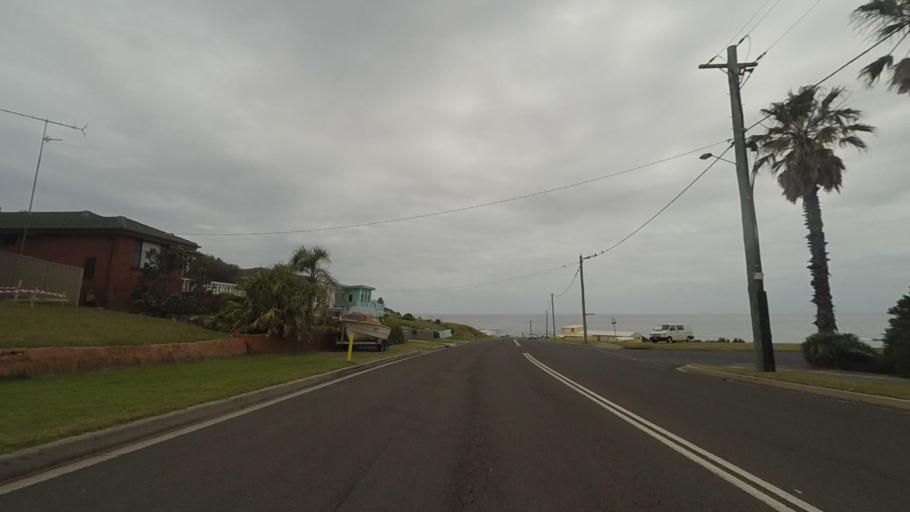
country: AU
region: New South Wales
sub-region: Wollongong
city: Port Kembla
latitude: -34.4906
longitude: 150.9066
